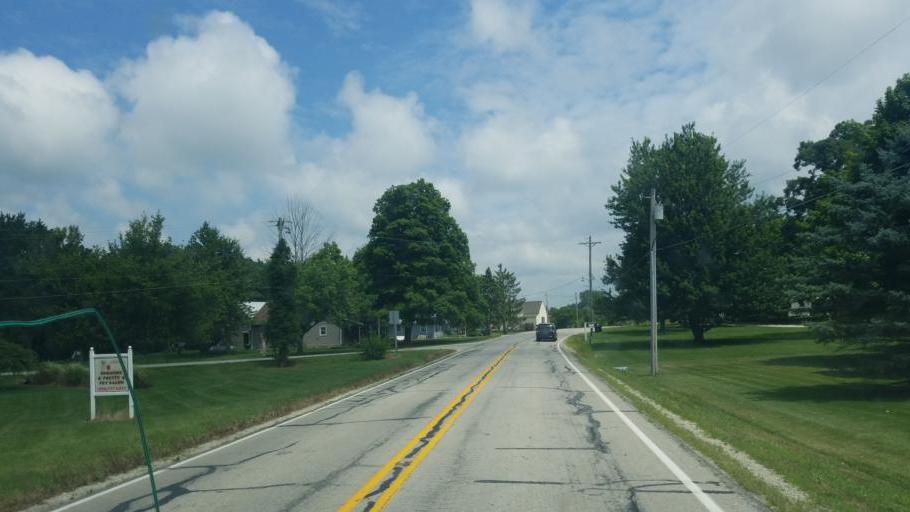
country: US
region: Indiana
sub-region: Huntington County
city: Warren
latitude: 40.6772
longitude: -85.4341
